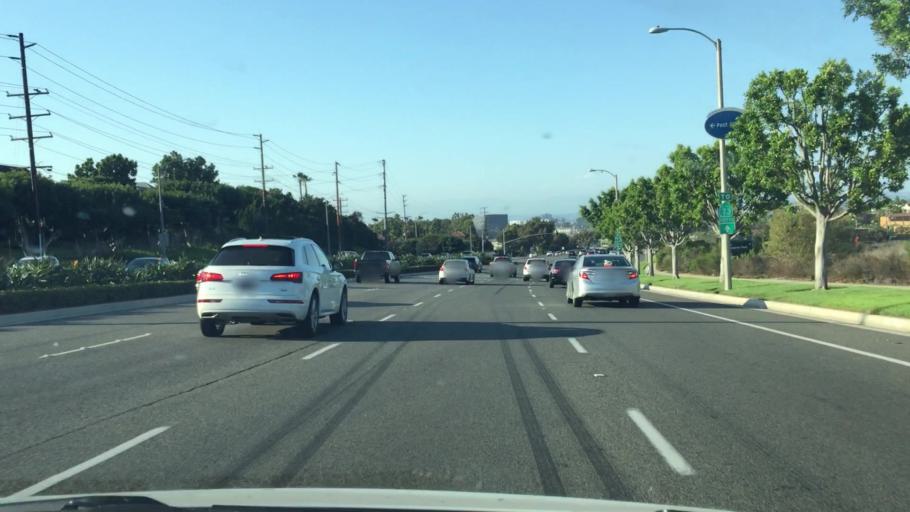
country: US
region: California
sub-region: Orange County
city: San Joaquin Hills
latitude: 33.6347
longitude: -117.8627
